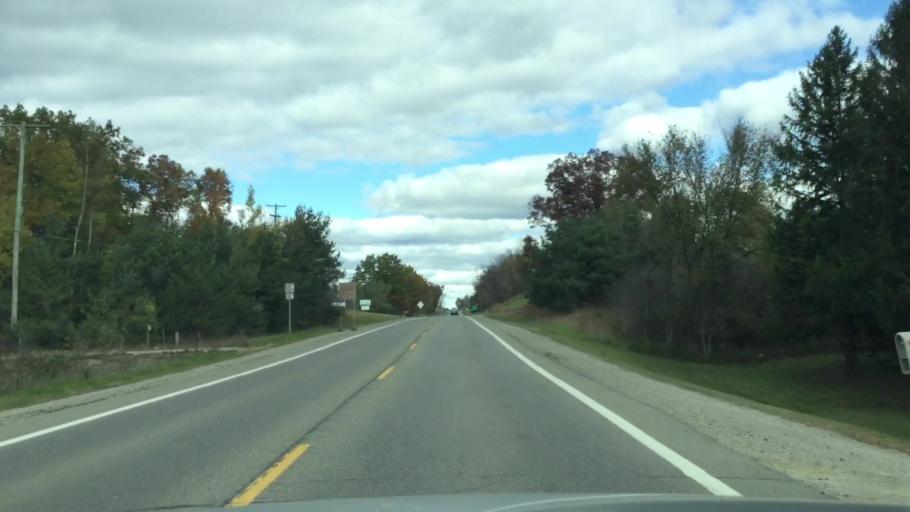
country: US
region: Michigan
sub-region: Lapeer County
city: Barnes Lake-Millers Lake
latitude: 43.1819
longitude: -83.3123
